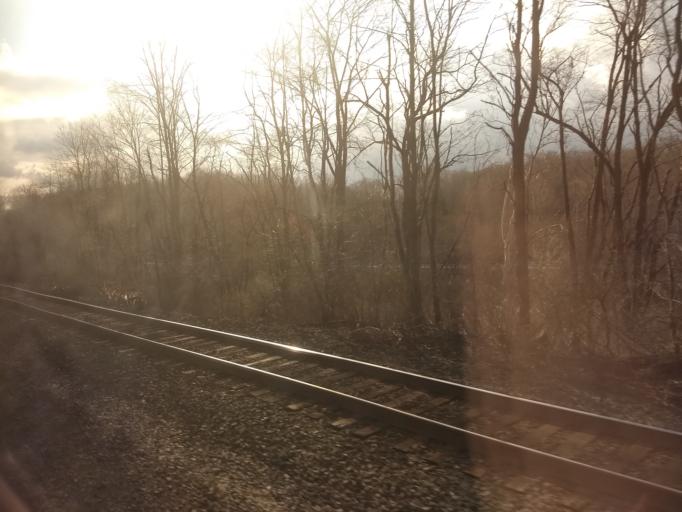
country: US
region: Pennsylvania
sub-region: Cambria County
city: Portage
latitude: 40.3791
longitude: -78.7415
